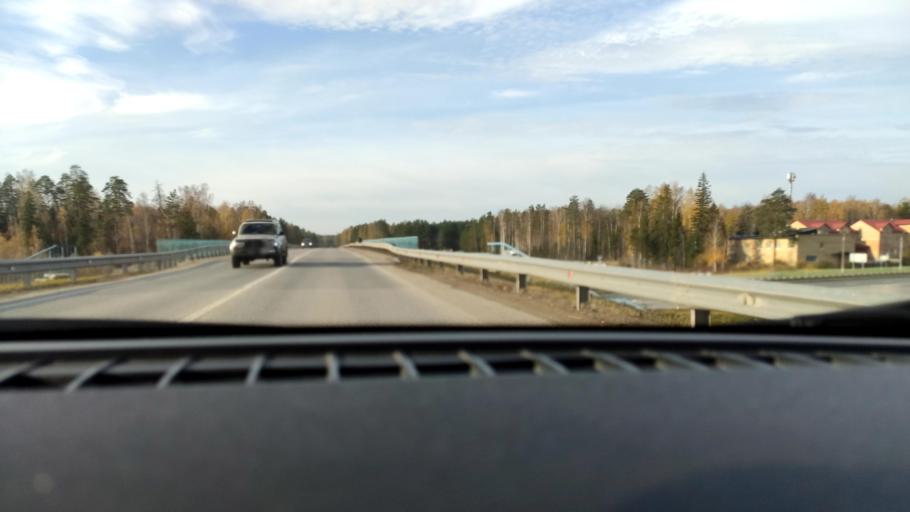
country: RU
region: Perm
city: Overyata
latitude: 58.0438
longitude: 55.8760
